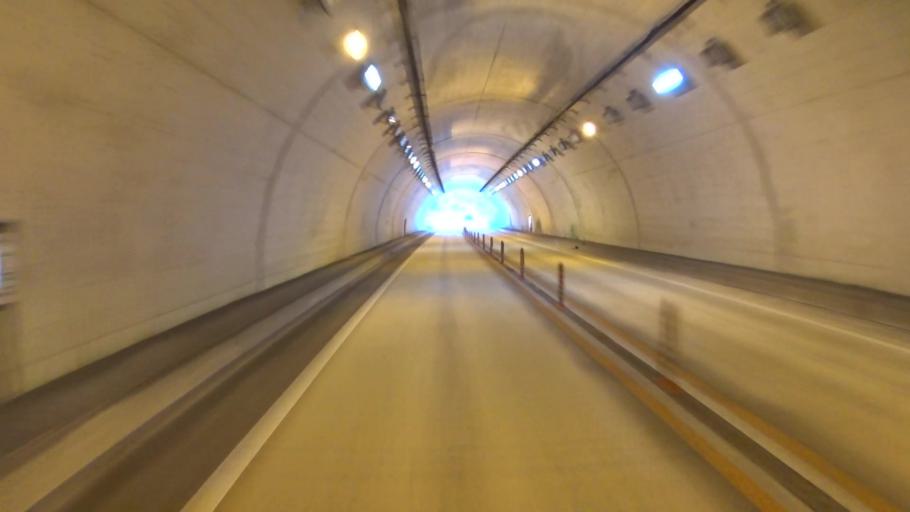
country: JP
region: Kyoto
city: Ayabe
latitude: 35.3169
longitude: 135.3190
